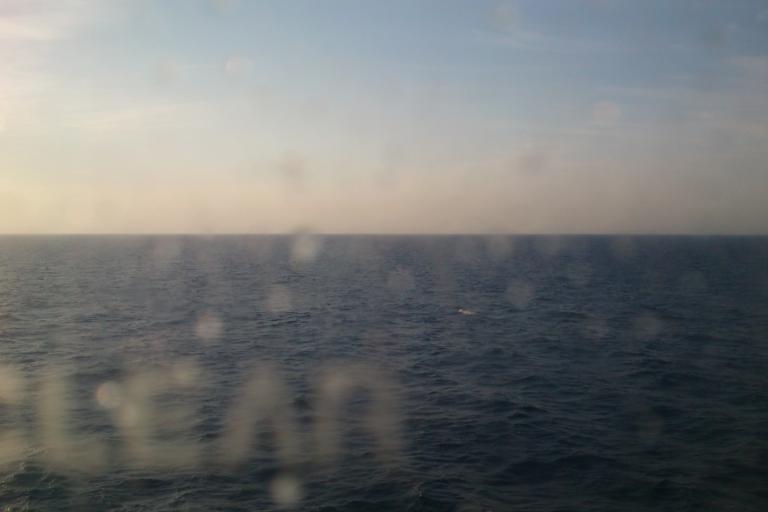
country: JP
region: Ishikawa
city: Nanao
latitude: 37.7299
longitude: 136.3949
